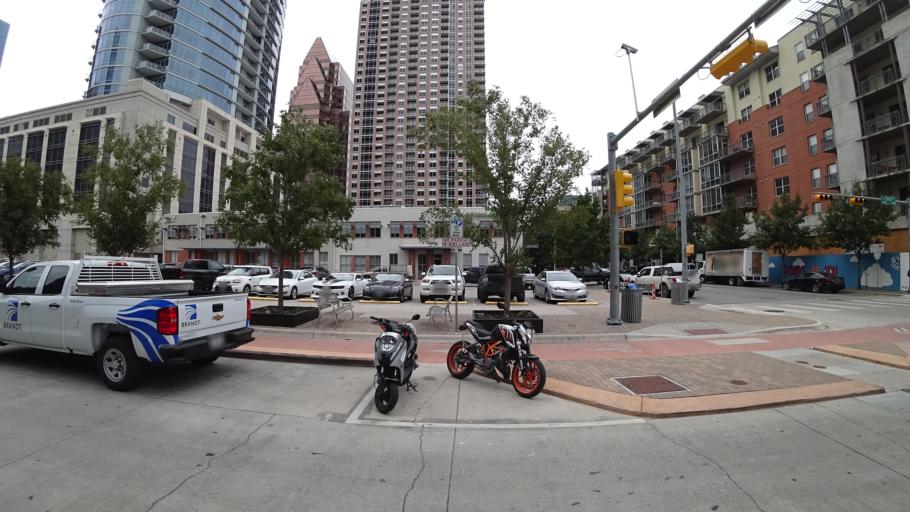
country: US
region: Texas
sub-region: Travis County
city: Austin
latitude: 30.2656
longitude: -97.7450
